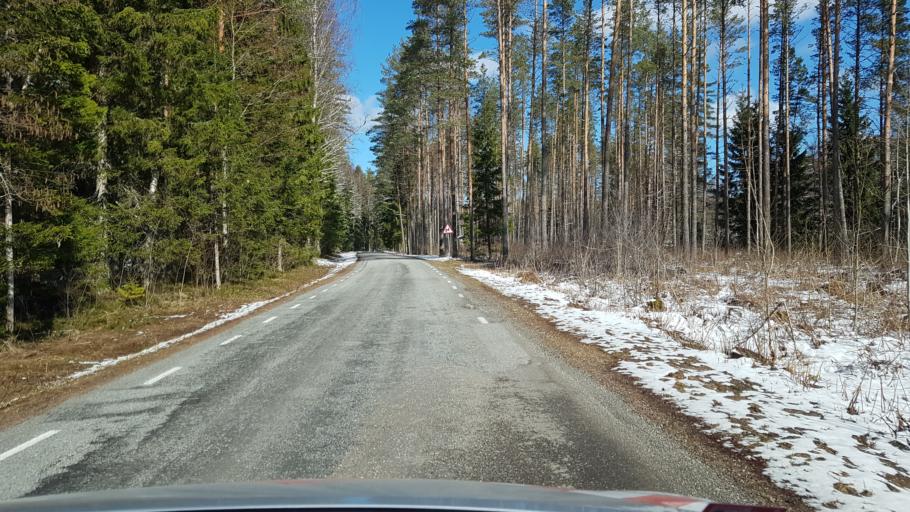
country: EE
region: Laeaene-Virumaa
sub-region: Kadrina vald
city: Kadrina
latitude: 59.5130
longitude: 25.9738
